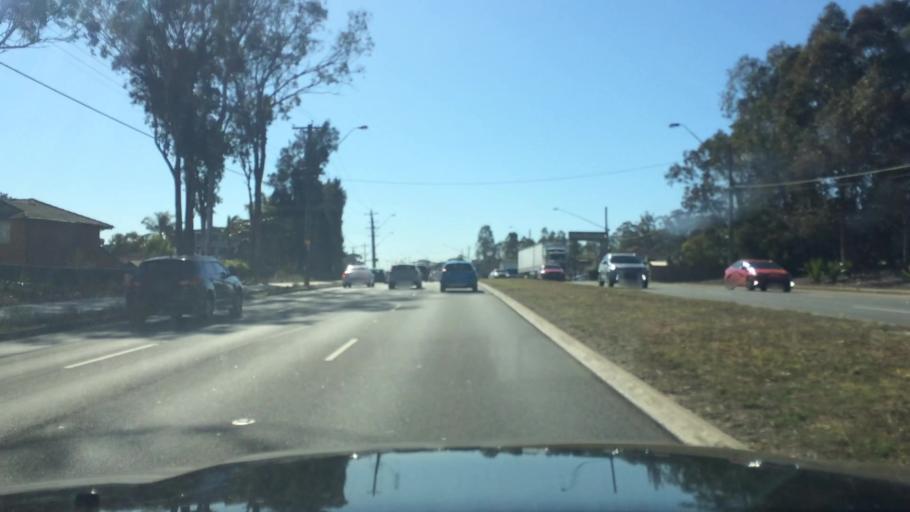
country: AU
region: New South Wales
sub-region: Campbelltown Municipality
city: Glenfield
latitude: -33.9518
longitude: 150.9024
